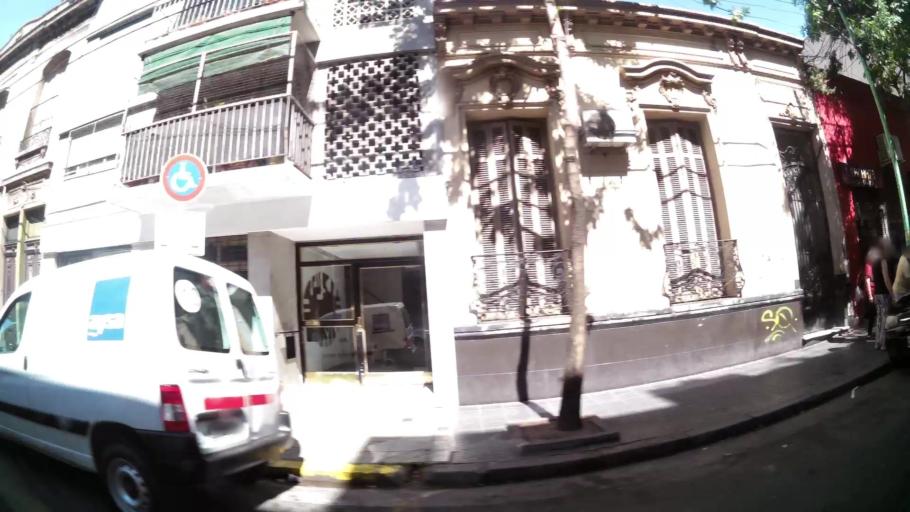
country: AR
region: Buenos Aires F.D.
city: Buenos Aires
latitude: -34.6242
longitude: -58.3844
